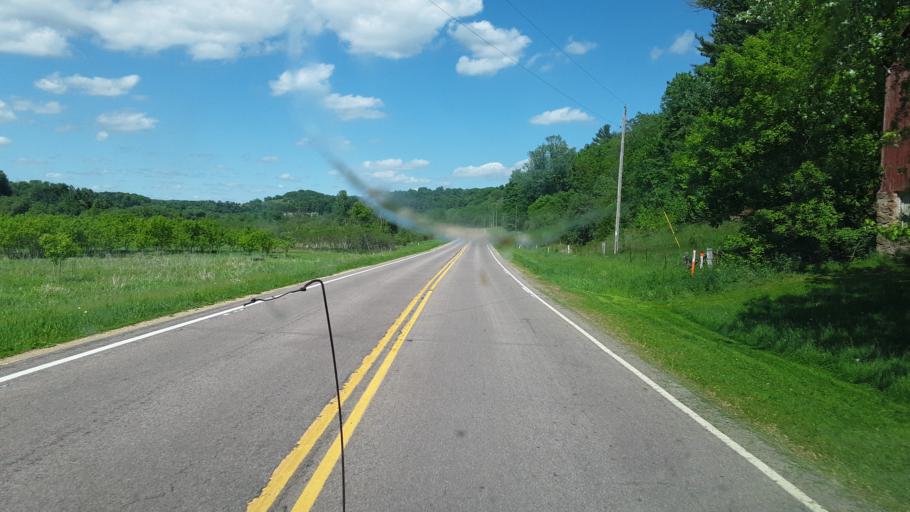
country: US
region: Wisconsin
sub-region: Richland County
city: Richland Center
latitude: 43.3867
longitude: -90.2477
